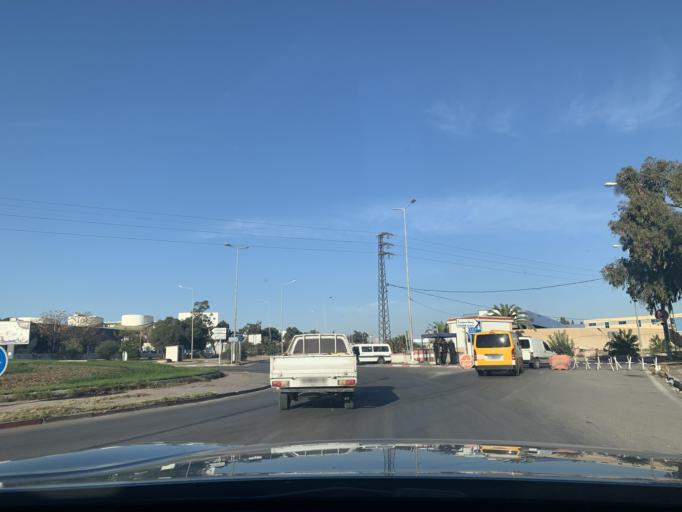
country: DZ
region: Souk Ahras
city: Souk Ahras
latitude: 36.3639
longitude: 8.0061
